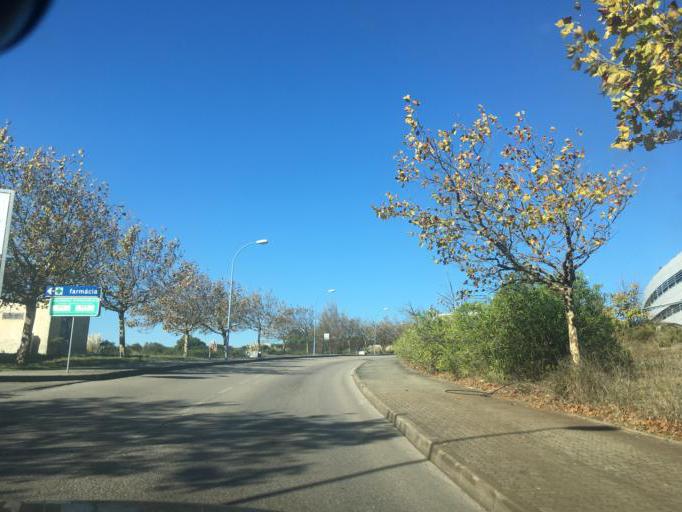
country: PT
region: Lisbon
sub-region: Oeiras
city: Porto Salvo
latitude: 38.7361
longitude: -9.3017
